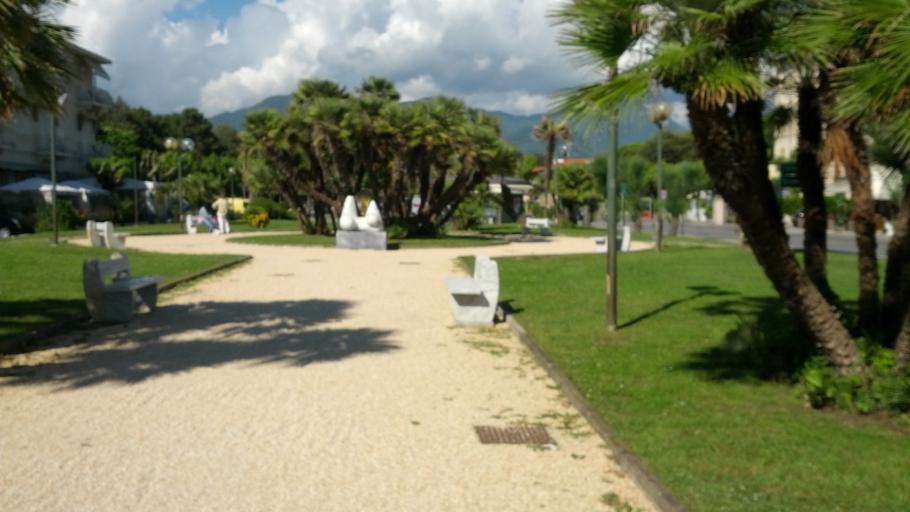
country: IT
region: Tuscany
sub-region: Provincia di Lucca
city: Pietrasanta
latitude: 43.9371
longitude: 10.1902
